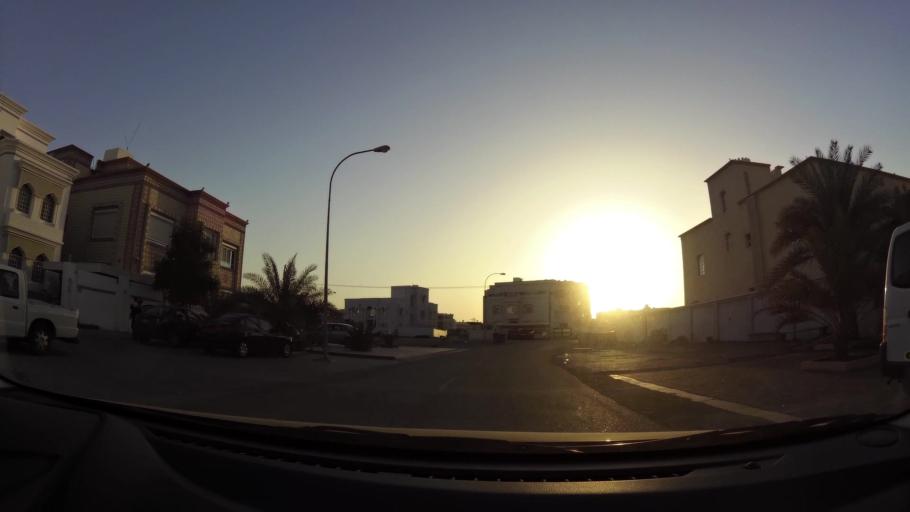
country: OM
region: Muhafazat Masqat
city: As Sib al Jadidah
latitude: 23.6135
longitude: 58.1993
